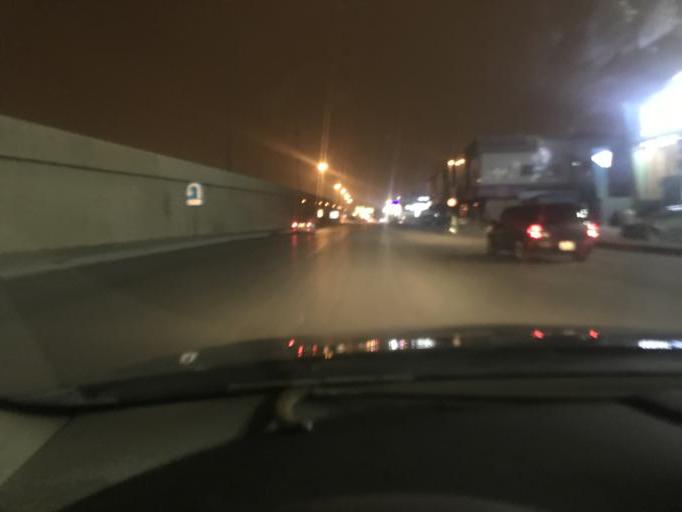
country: SA
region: Ar Riyad
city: Riyadh
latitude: 24.7925
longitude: 46.7002
